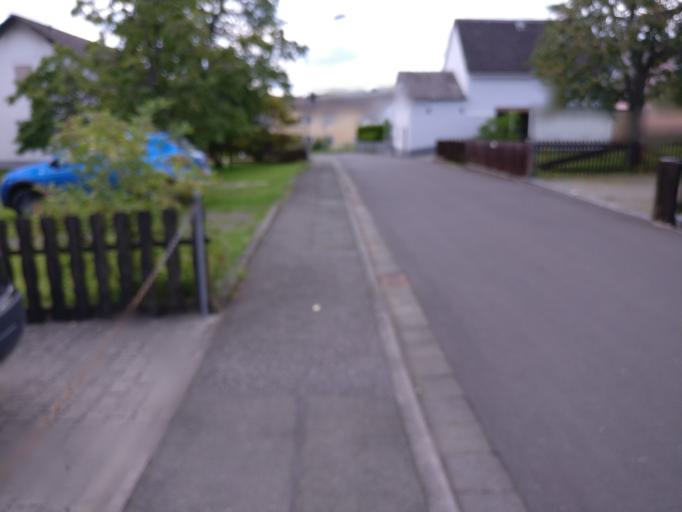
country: DE
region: Hesse
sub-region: Regierungsbezirk Giessen
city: Greifenstein
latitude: 50.6219
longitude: 8.2924
